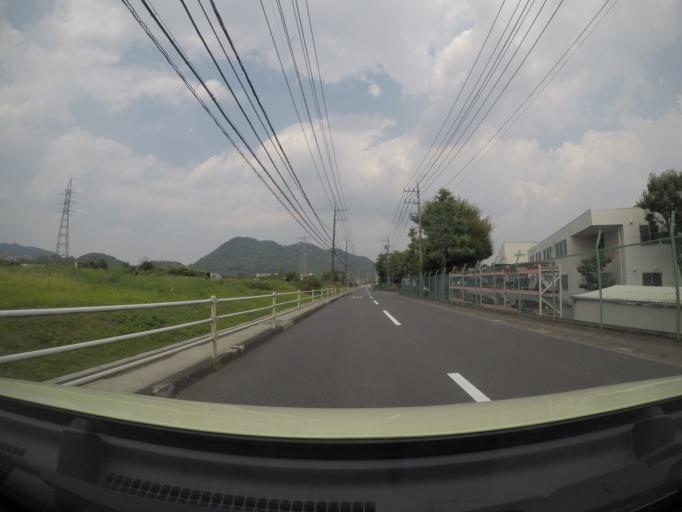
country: JP
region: Tokyo
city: Hachioji
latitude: 35.5724
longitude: 139.2699
